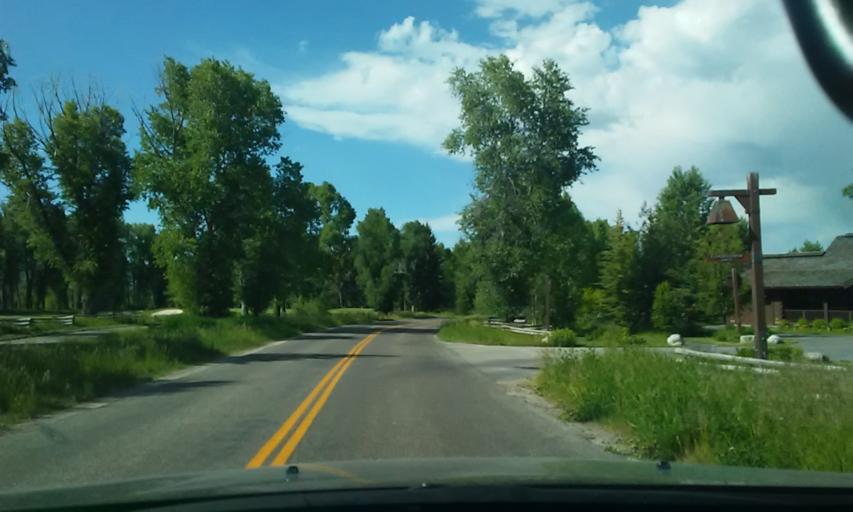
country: US
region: Wyoming
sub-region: Teton County
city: Jackson
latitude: 43.5656
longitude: -110.7477
